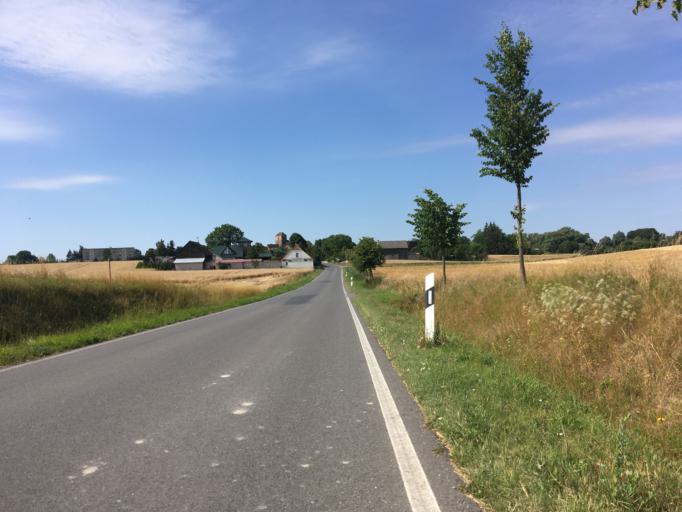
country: DE
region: Brandenburg
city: Gramzow
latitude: 53.2474
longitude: 14.0496
